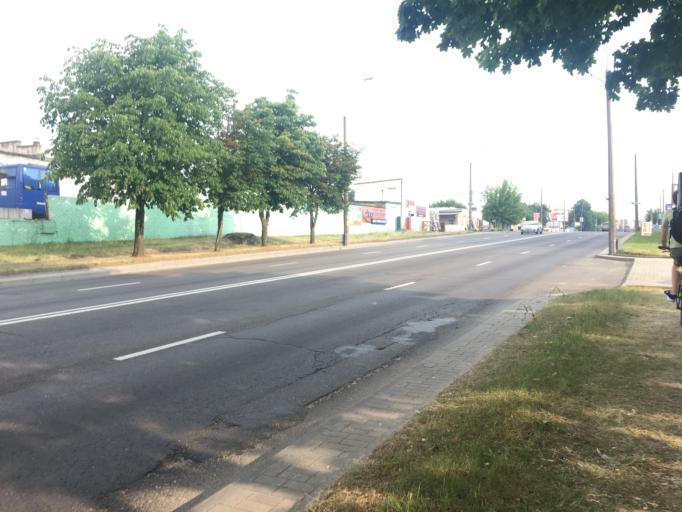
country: BY
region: Grodnenskaya
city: Hrodna
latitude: 53.6572
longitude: 23.8305
